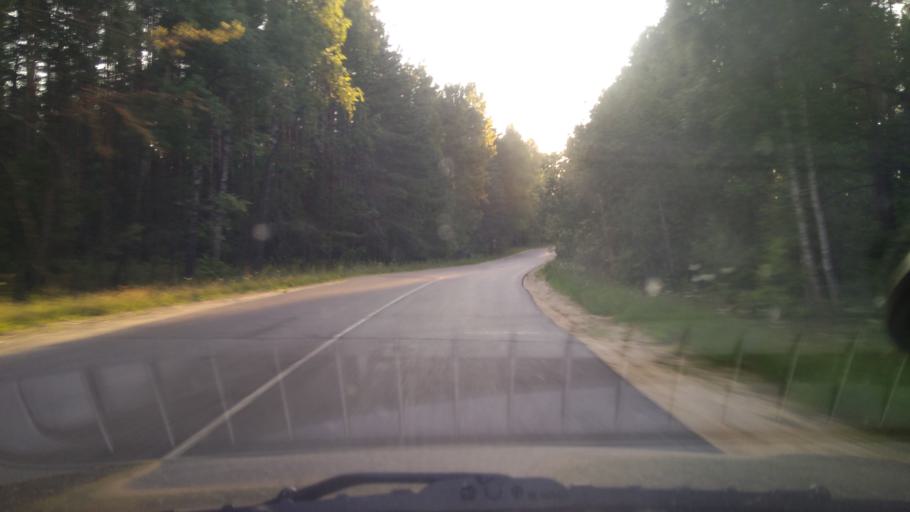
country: BY
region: Brest
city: Nyakhachava
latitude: 52.6023
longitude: 25.0904
